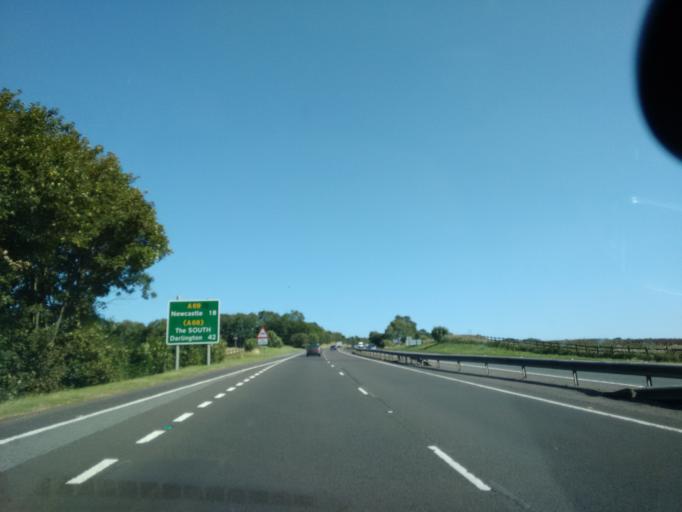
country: GB
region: England
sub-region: Northumberland
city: Corbridge
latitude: 54.9837
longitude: -2.0132
